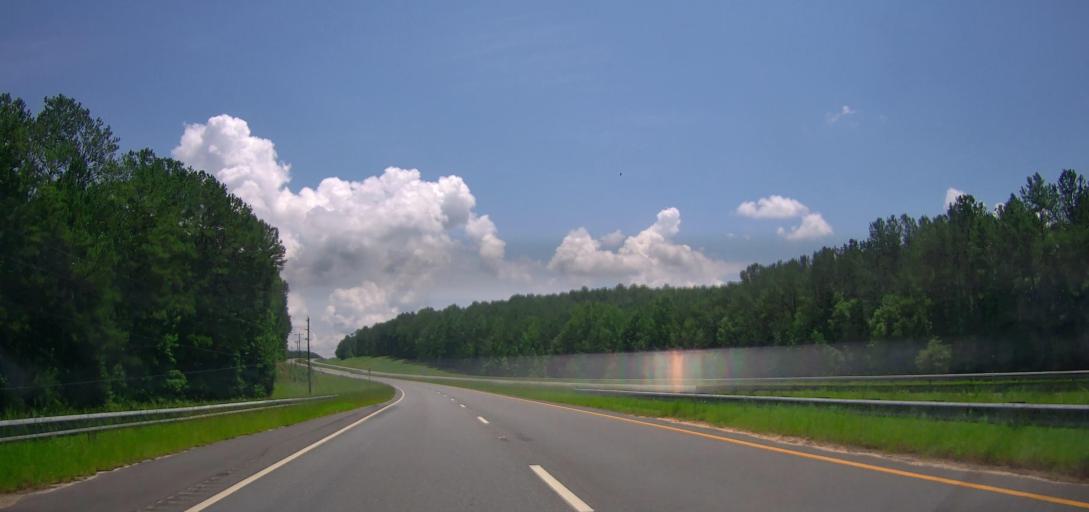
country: US
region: Georgia
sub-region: Upson County
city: Thomaston
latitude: 32.7946
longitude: -84.2649
